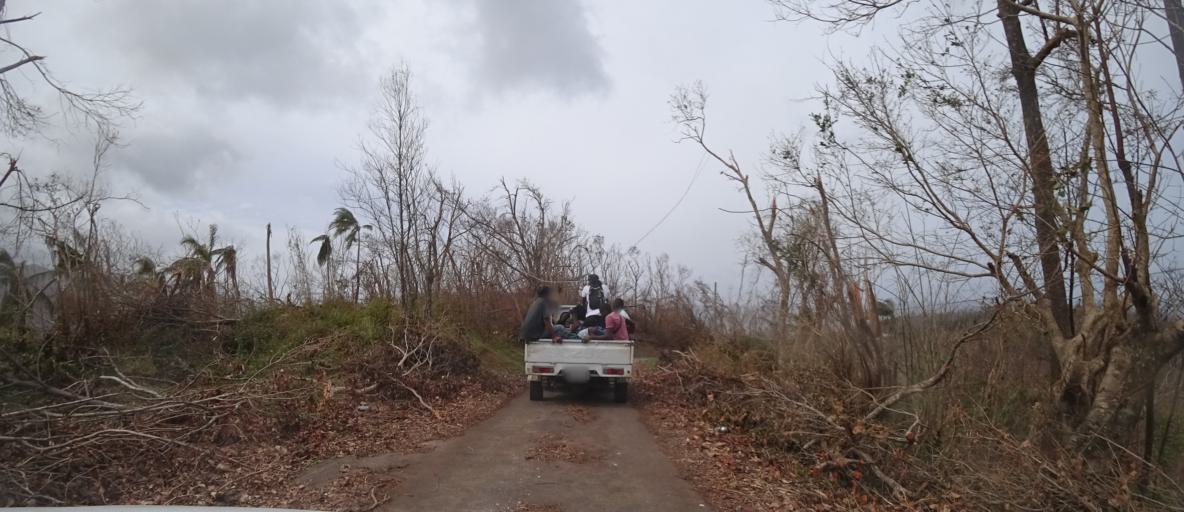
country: DM
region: Saint Andrew
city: Calibishie
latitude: 15.5876
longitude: -61.3714
